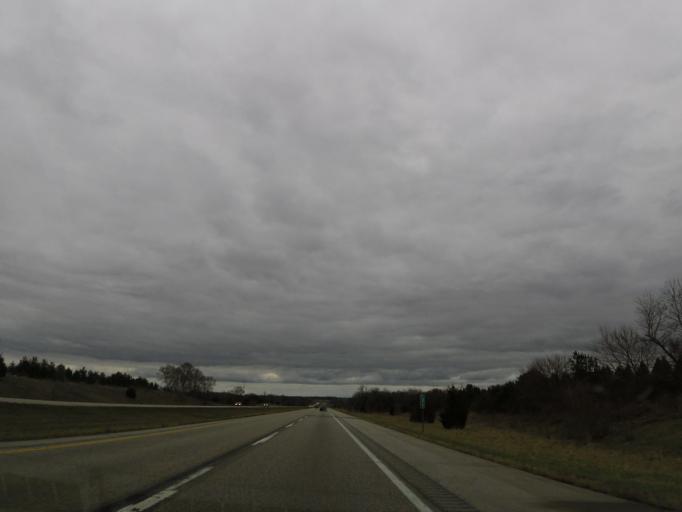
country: US
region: Iowa
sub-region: Linn County
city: Robins
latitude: 42.1217
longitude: -91.7150
